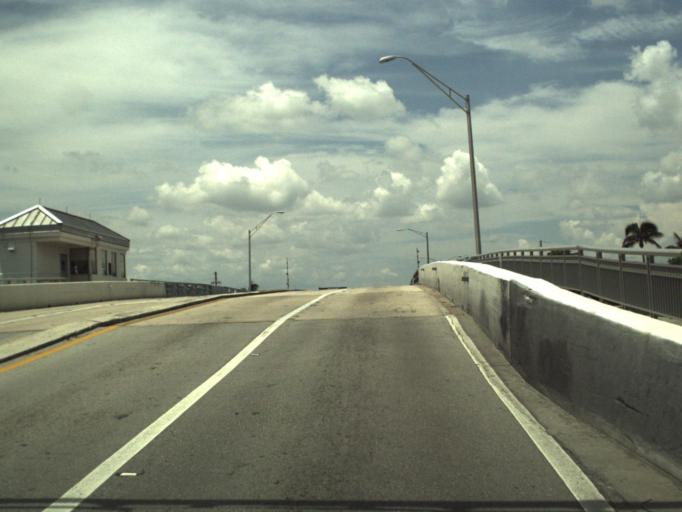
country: US
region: Florida
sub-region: Broward County
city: Terra Mar
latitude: 26.2319
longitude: -80.0931
